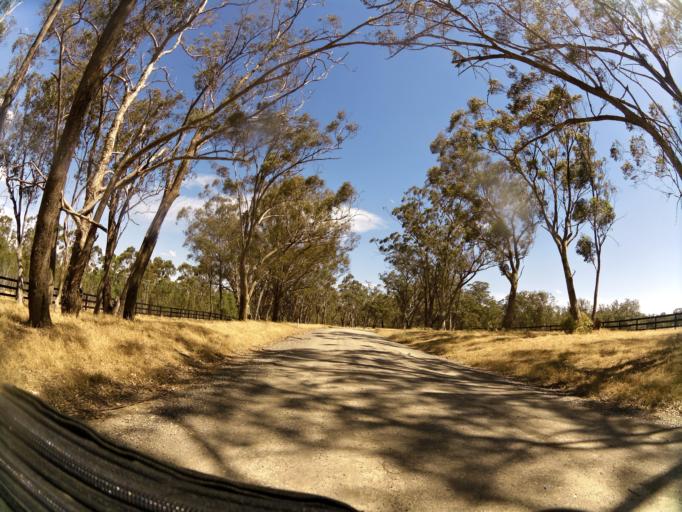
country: AU
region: Victoria
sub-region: Campaspe
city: Kyabram
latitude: -36.8279
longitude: 145.0779
